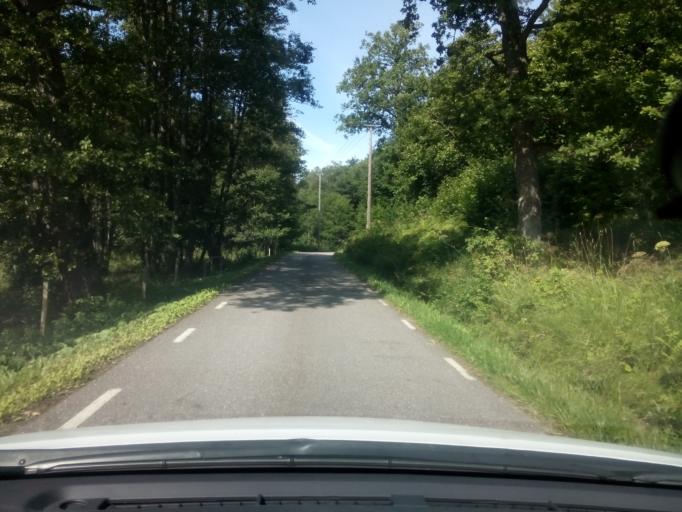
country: SE
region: Soedermanland
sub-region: Trosa Kommun
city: Trosa
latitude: 58.8034
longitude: 17.3676
